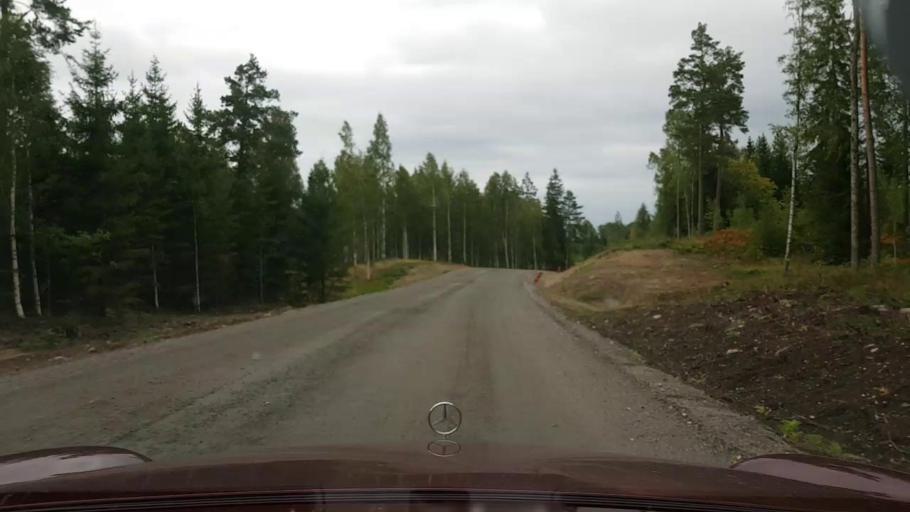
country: SE
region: Vaestra Goetaland
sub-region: Karlsborgs Kommun
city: Karlsborg
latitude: 58.7069
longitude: 14.5018
